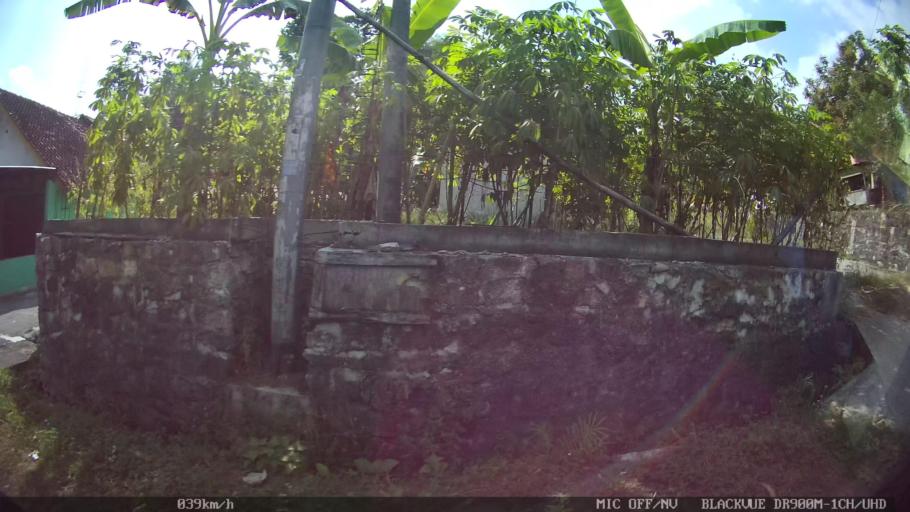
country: ID
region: Daerah Istimewa Yogyakarta
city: Kasihan
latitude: -7.8408
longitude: 110.3118
